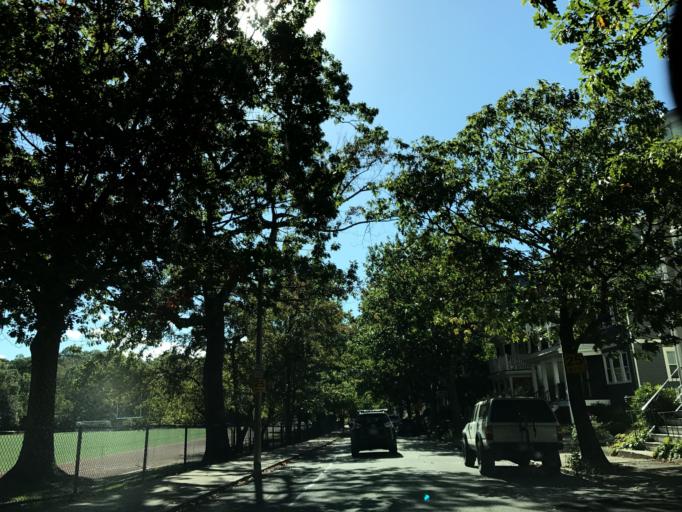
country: US
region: Massachusetts
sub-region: Norfolk County
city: Brookline
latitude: 42.3255
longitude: -71.1194
